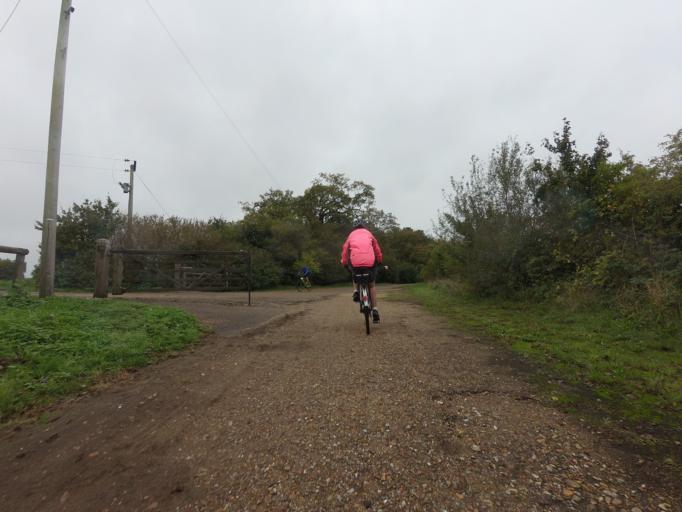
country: GB
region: England
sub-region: Norfolk
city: Dersingham
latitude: 52.8035
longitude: 0.4846
